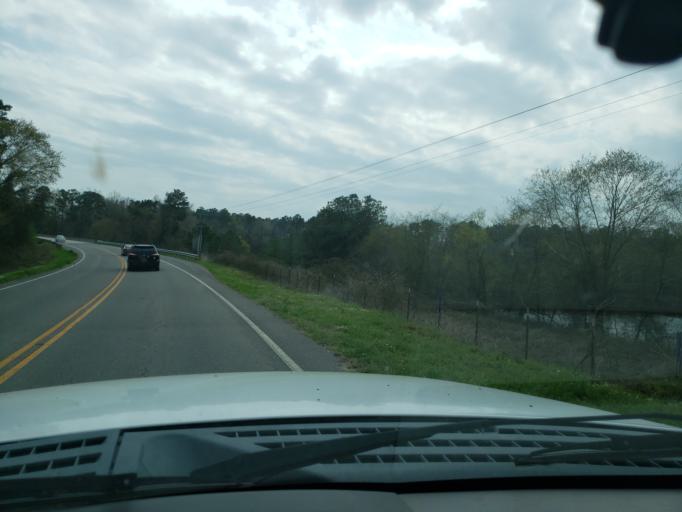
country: US
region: North Carolina
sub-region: Duplin County
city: Beulaville
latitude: 34.7855
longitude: -77.8380
